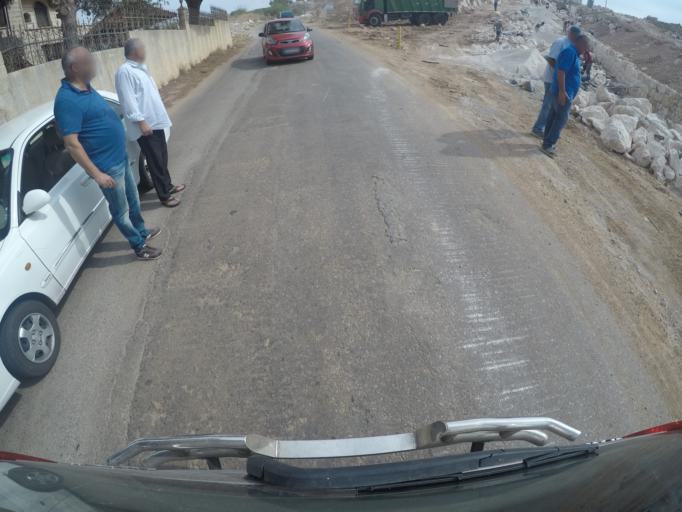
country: LB
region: Mont-Liban
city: Beit ed Dine
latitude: 33.7335
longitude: 35.4627
